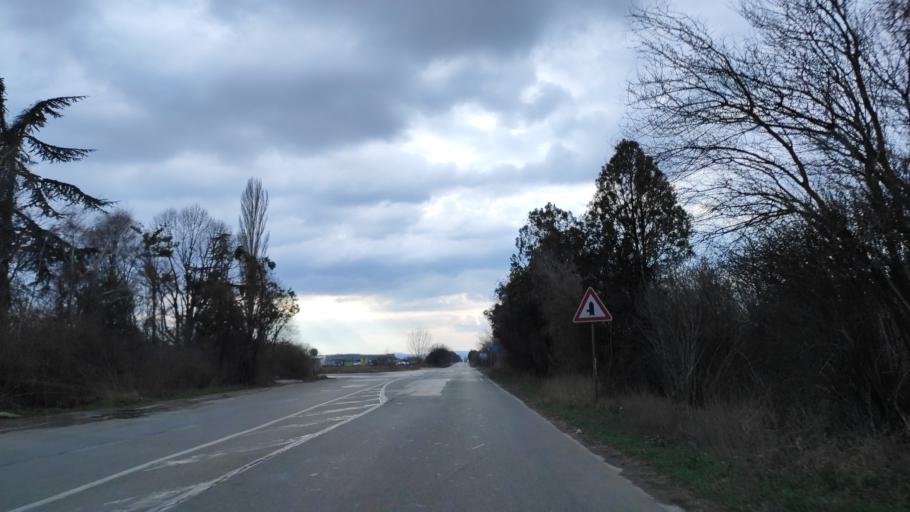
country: BG
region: Varna
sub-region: Obshtina Aksakovo
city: Aksakovo
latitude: 43.2294
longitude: 27.8248
